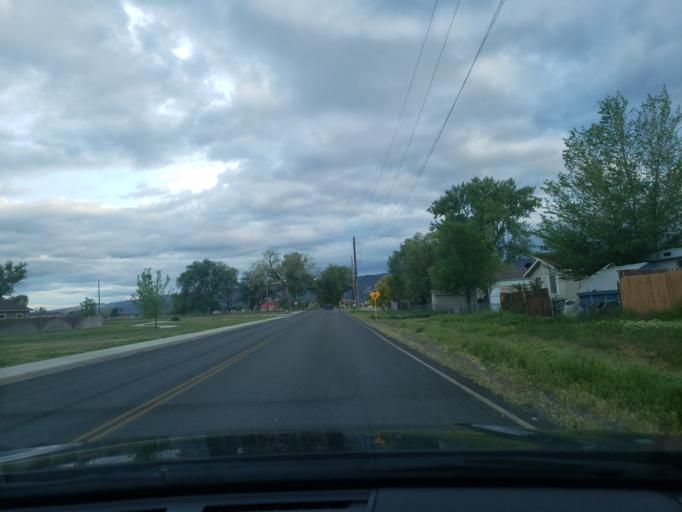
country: US
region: Colorado
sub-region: Mesa County
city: Fruita
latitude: 39.1659
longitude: -108.7105
